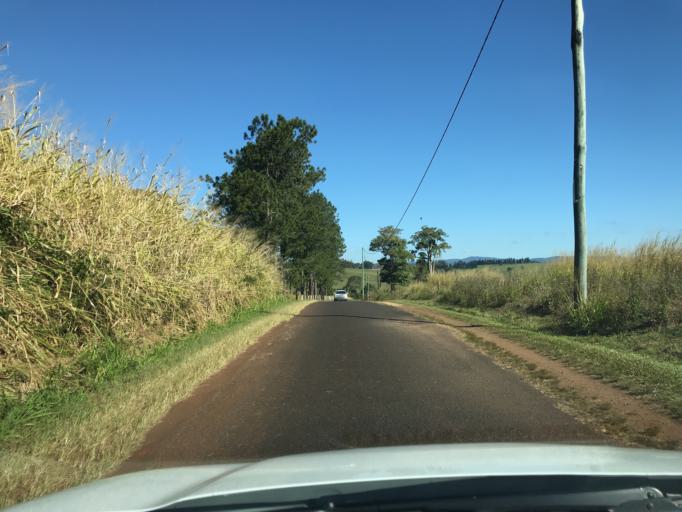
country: AU
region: Queensland
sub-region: Tablelands
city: Atherton
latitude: -17.2924
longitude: 145.5447
